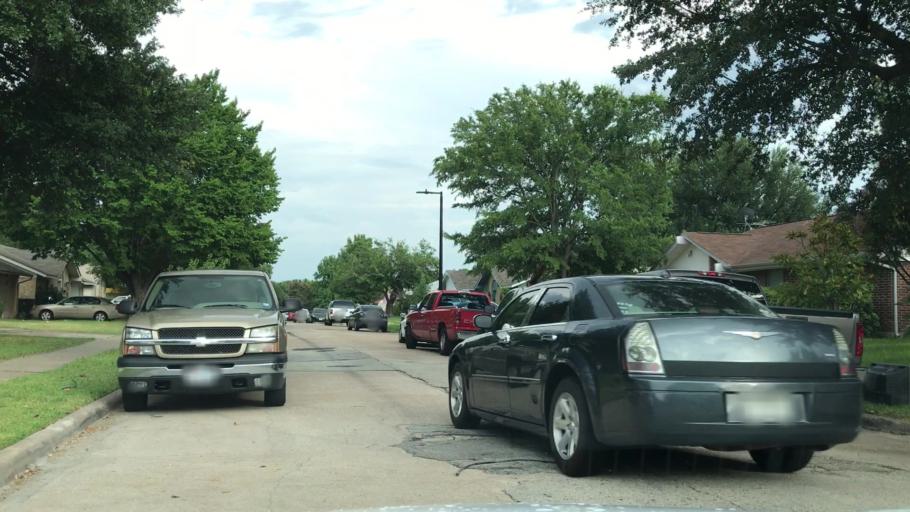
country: US
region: Texas
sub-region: Dallas County
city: Garland
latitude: 32.8618
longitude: -96.6376
